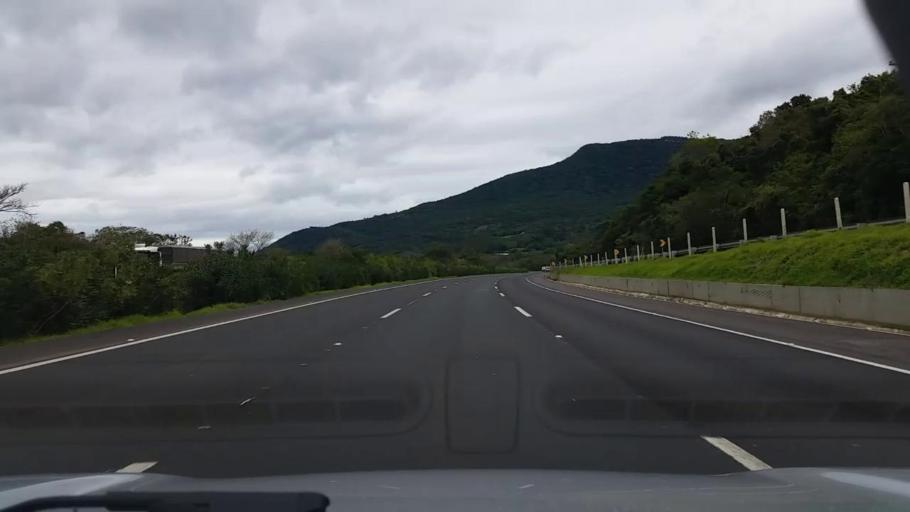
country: BR
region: Rio Grande do Sul
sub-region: Osorio
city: Osorio
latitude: -29.8961
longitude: -50.3490
